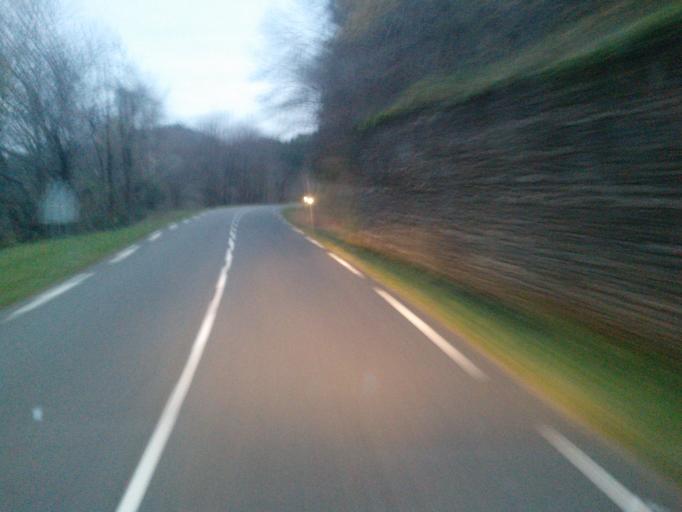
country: FR
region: Languedoc-Roussillon
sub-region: Departement du Gard
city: Saint-Jean-du-Gard
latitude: 44.1303
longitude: 3.7972
